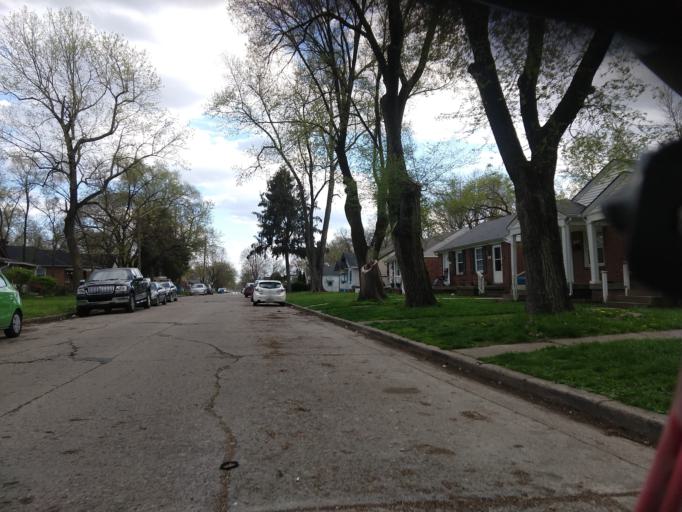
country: US
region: Indiana
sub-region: Marion County
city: Broad Ripple
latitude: 39.8359
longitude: -86.1277
